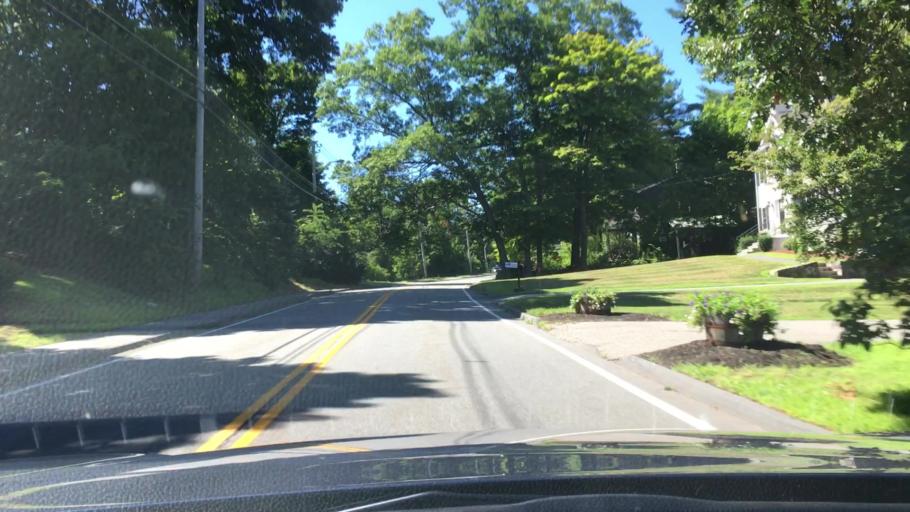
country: US
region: Massachusetts
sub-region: Middlesex County
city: Billerica
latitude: 42.5715
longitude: -71.2622
